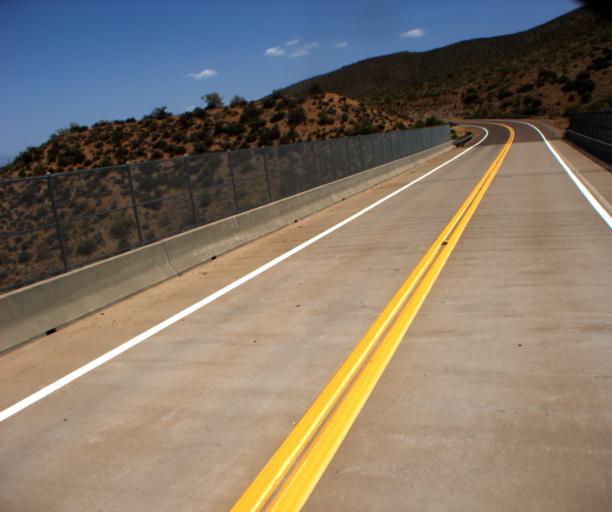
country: US
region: Arizona
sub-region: Gila County
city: Tonto Basin
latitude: 33.7015
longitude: -111.1893
